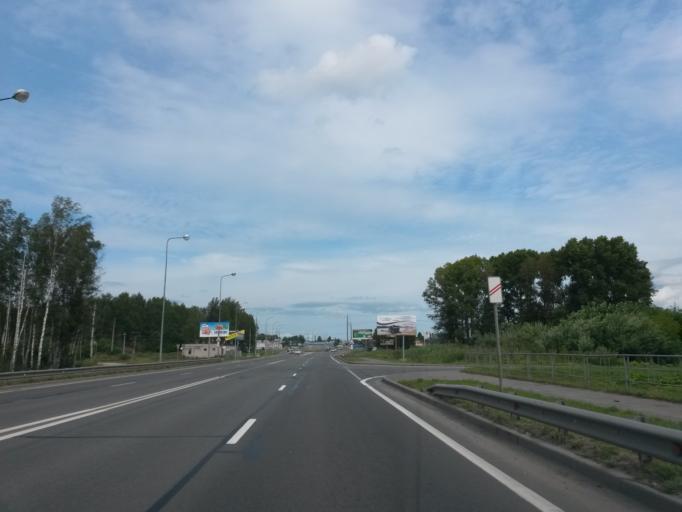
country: RU
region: Jaroslavl
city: Yaroslavl
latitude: 57.6930
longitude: 39.8987
